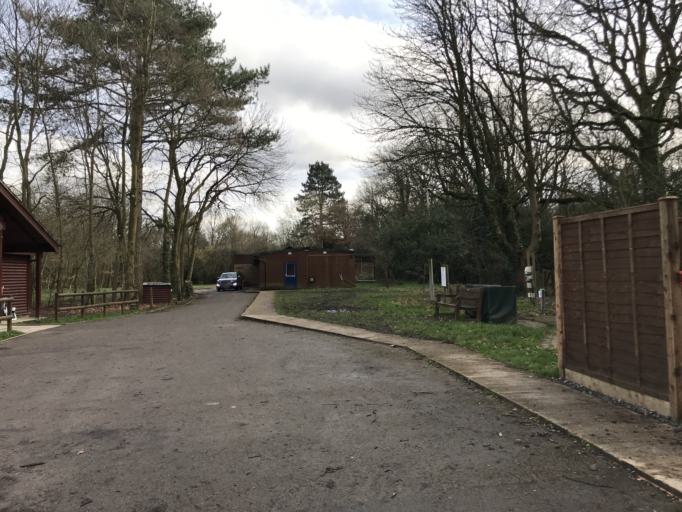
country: GB
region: England
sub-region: Buckinghamshire
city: Chalfont Saint Peter
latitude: 51.6055
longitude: -0.5410
